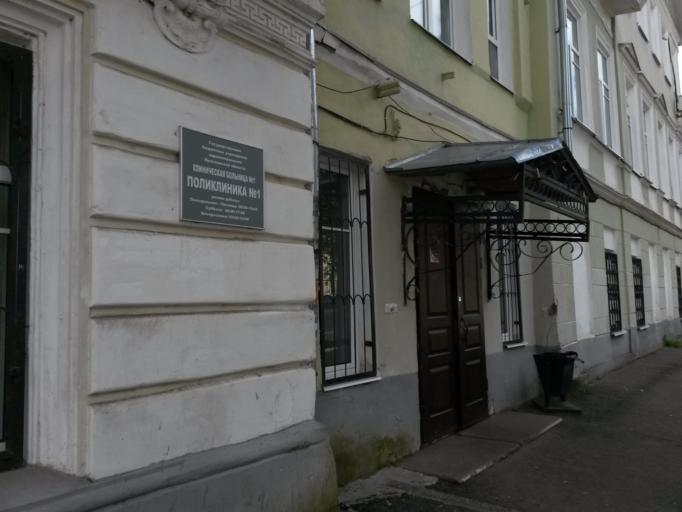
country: RU
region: Jaroslavl
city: Yaroslavl
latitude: 57.6269
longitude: 39.8815
